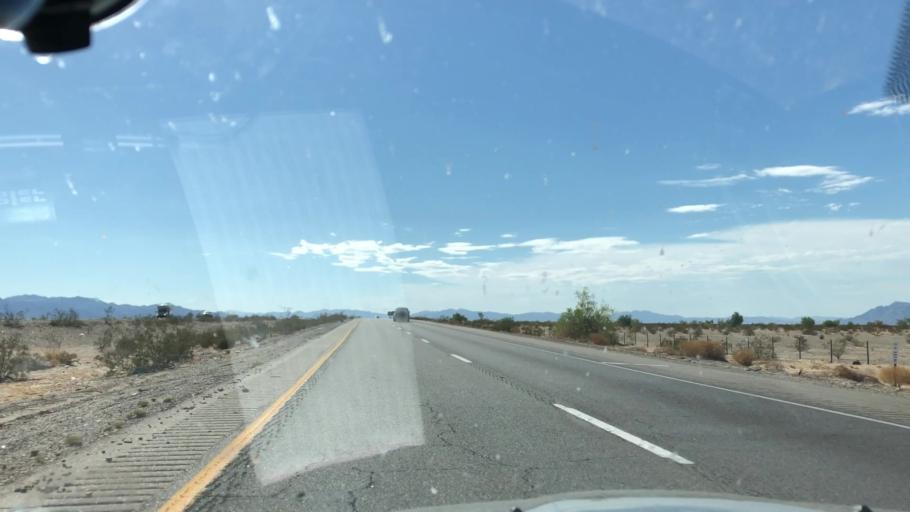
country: US
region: California
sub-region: Riverside County
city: Mesa Verde
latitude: 33.6507
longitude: -115.1355
